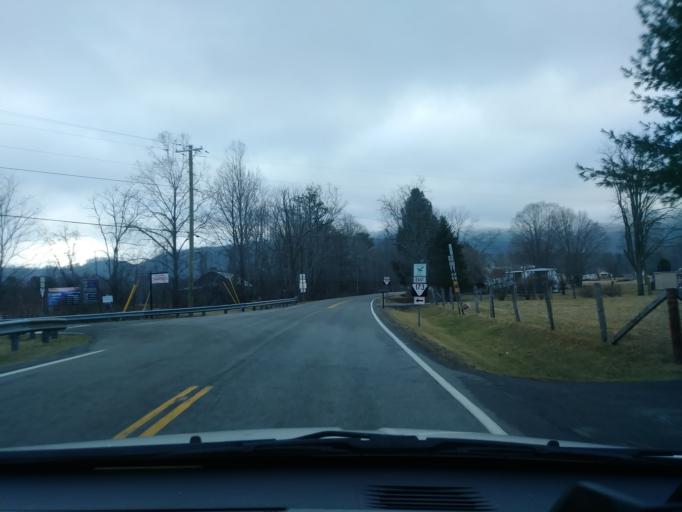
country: US
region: Tennessee
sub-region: Unicoi County
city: Unicoi
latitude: 36.1792
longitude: -82.2623
